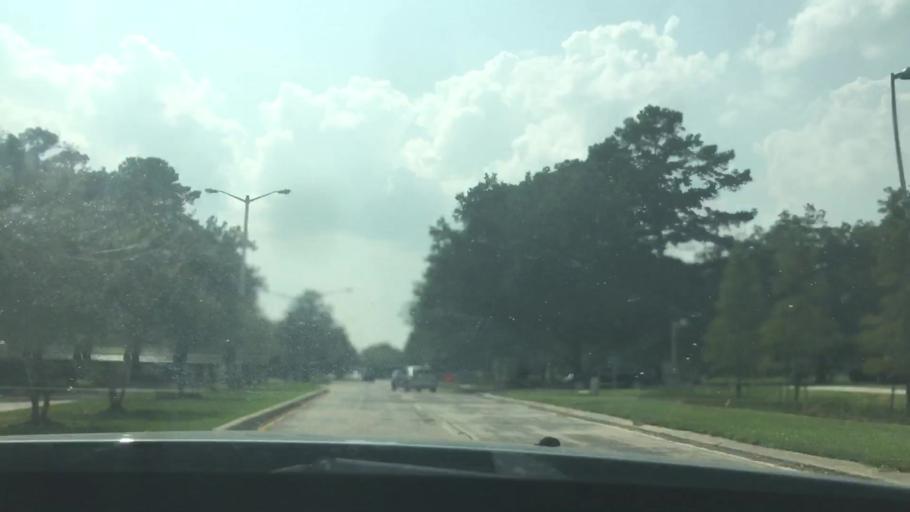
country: US
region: Louisiana
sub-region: East Baton Rouge Parish
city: Westminster
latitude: 30.4424
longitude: -91.1060
